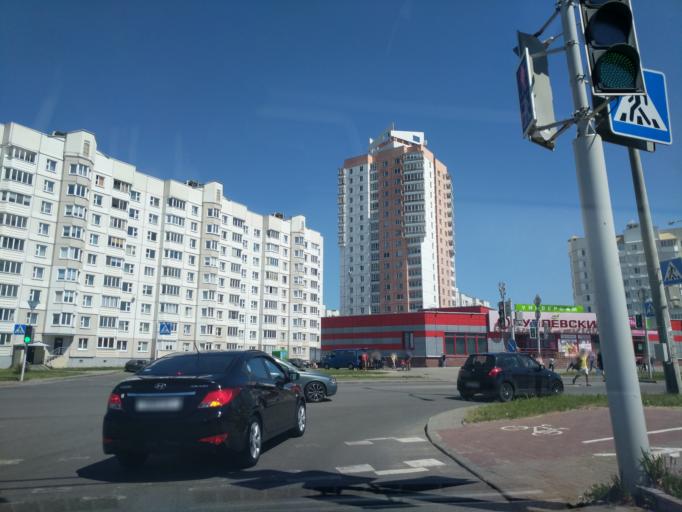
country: BY
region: Minsk
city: Zhdanovichy
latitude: 53.9120
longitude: 27.4155
